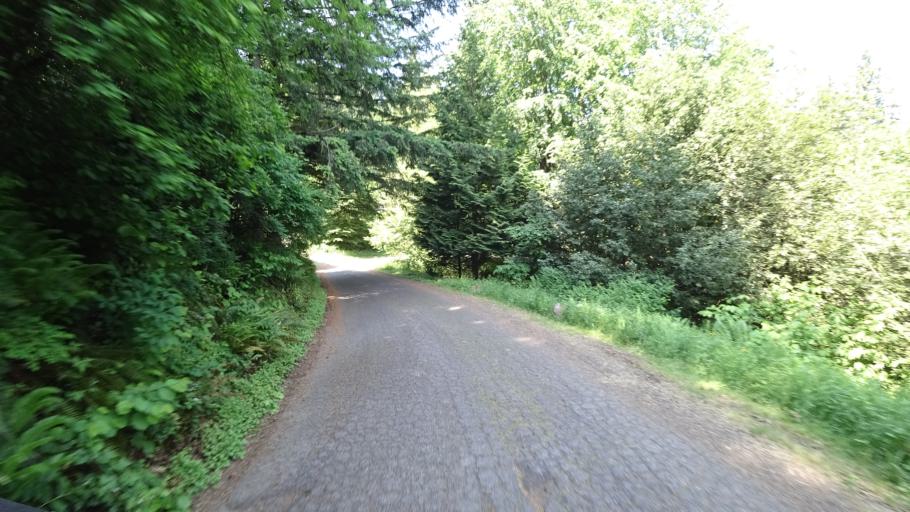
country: US
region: Oregon
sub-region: Multnomah County
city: Portland
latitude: 45.5149
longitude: -122.7144
